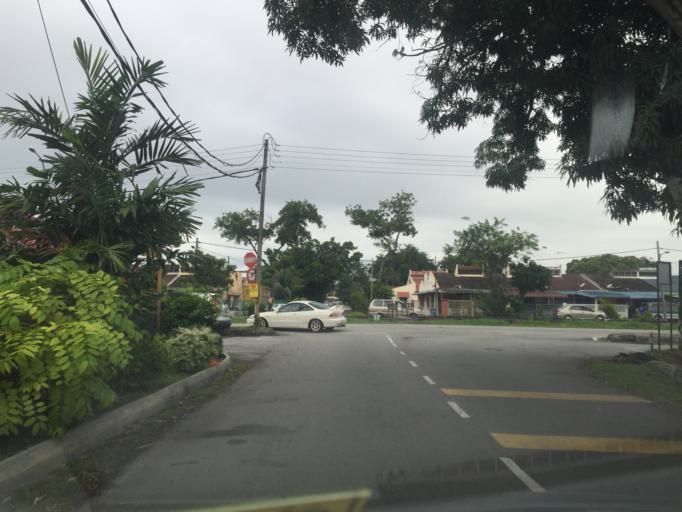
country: MY
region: Selangor
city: Klang
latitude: 3.0237
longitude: 101.4322
